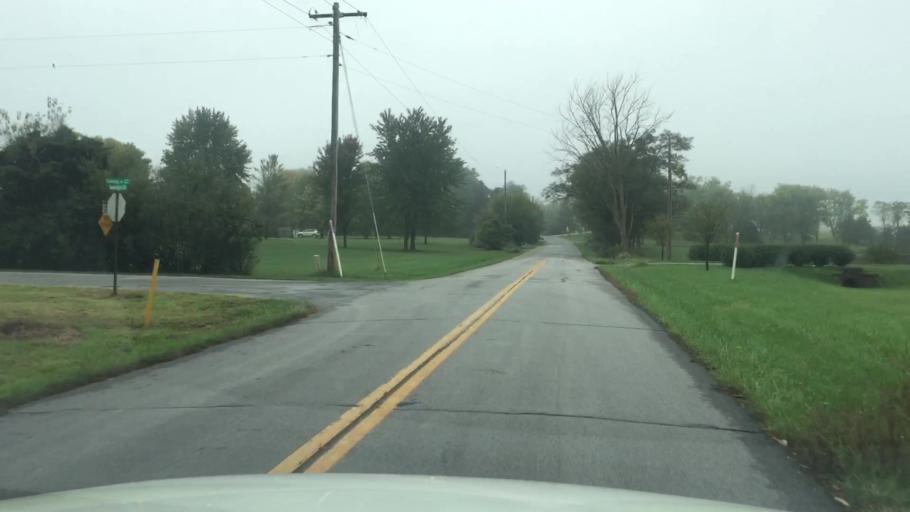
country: US
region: Missouri
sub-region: Boone County
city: Ashland
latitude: 38.8499
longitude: -92.3060
